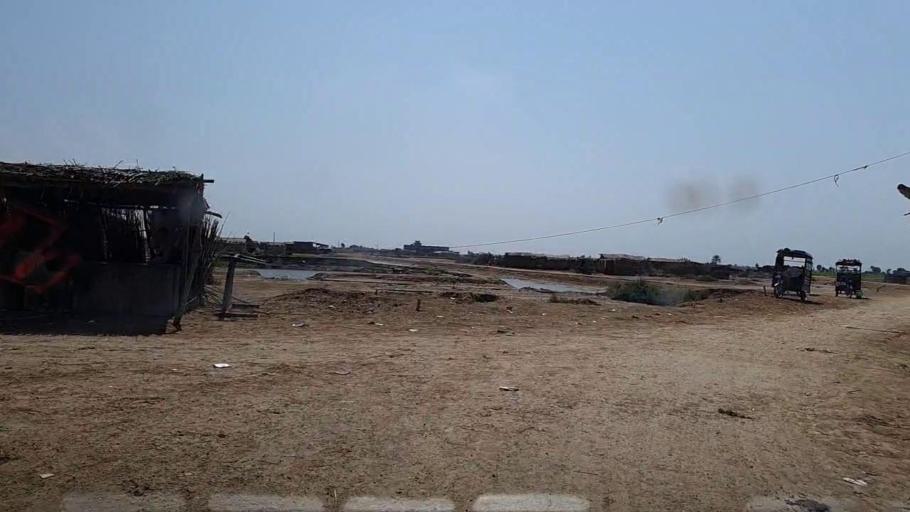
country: PK
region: Sindh
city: Kario
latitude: 24.6361
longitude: 68.4904
